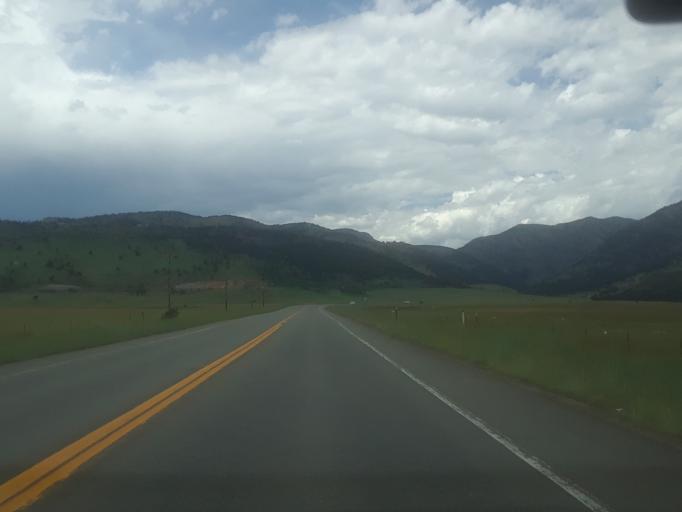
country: US
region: Colorado
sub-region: Jefferson County
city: Golden
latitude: 39.8664
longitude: -105.2455
